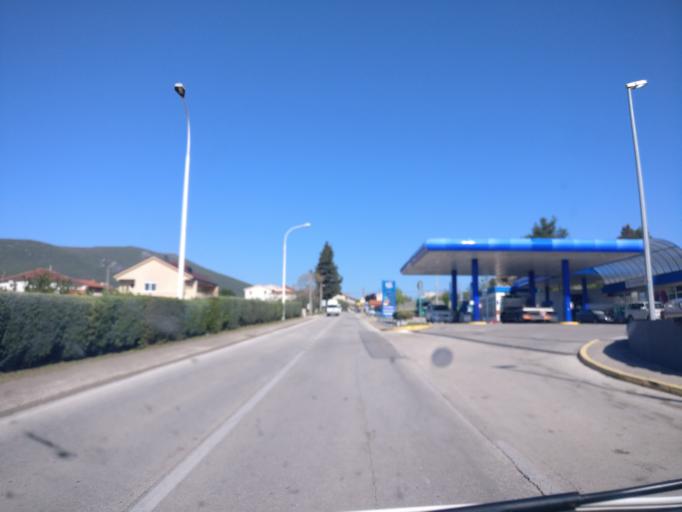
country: BA
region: Federation of Bosnia and Herzegovina
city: Capljina
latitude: 43.1208
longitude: 17.6866
